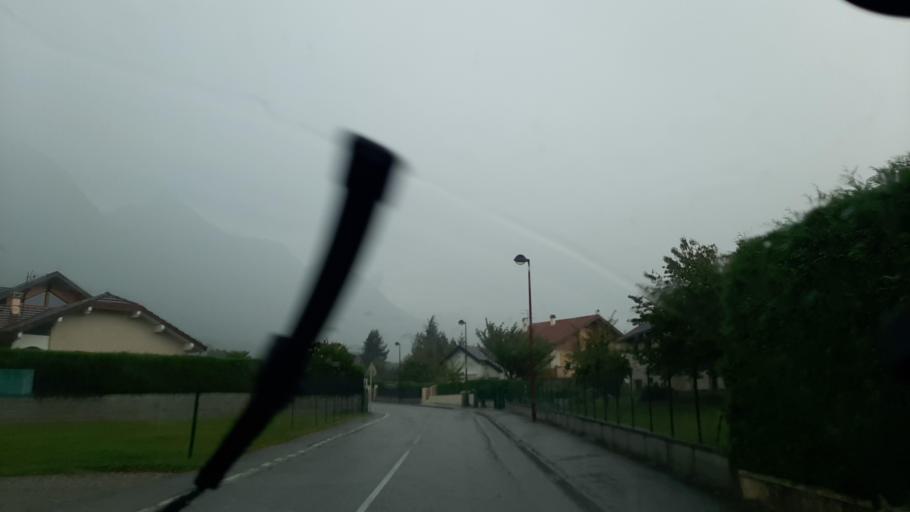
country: FR
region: Rhone-Alpes
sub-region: Departement de la Savoie
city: Gilly-sur-Isere
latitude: 45.6635
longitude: 6.3521
